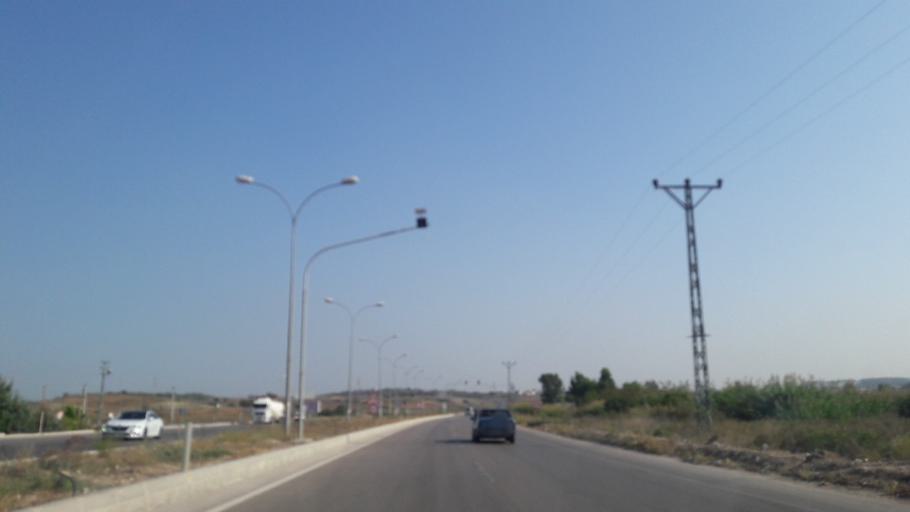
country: TR
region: Adana
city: Yuregir
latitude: 37.0600
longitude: 35.4446
